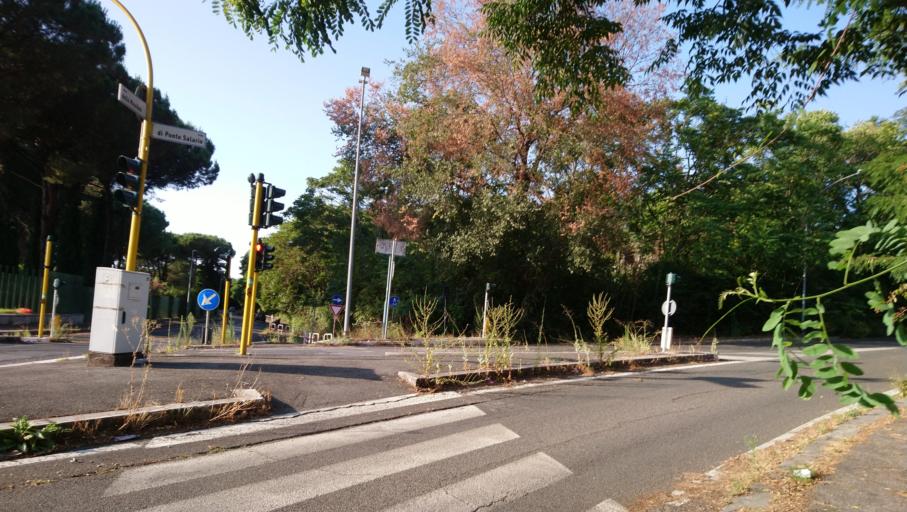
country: IT
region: Latium
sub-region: Citta metropolitana di Roma Capitale
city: Rome
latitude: 41.9359
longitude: 12.4965
